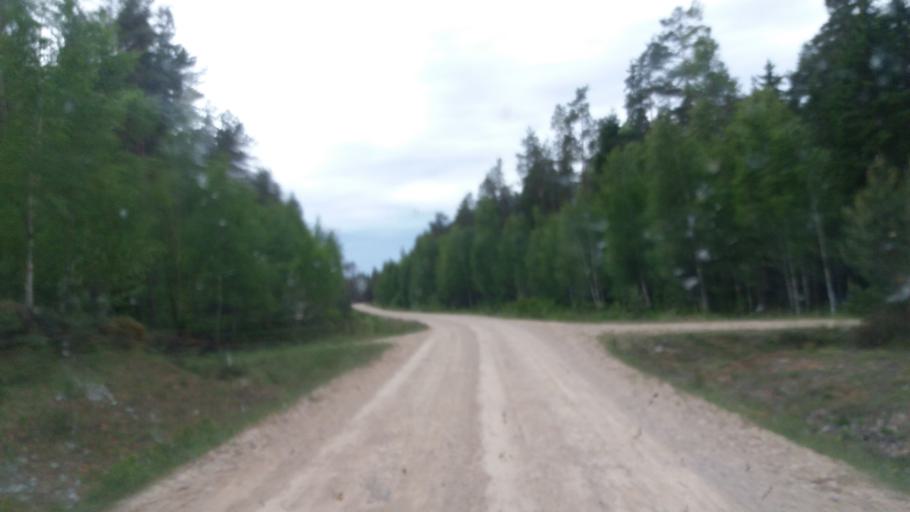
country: LV
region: Kuldigas Rajons
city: Kuldiga
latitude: 57.1532
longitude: 22.1217
